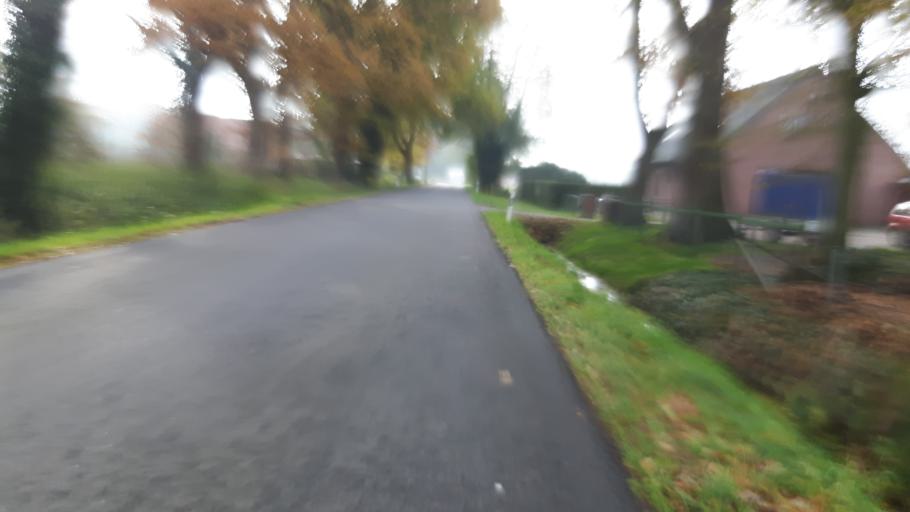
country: DE
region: Lower Saxony
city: Delmenhorst
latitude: 53.0189
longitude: 8.5872
